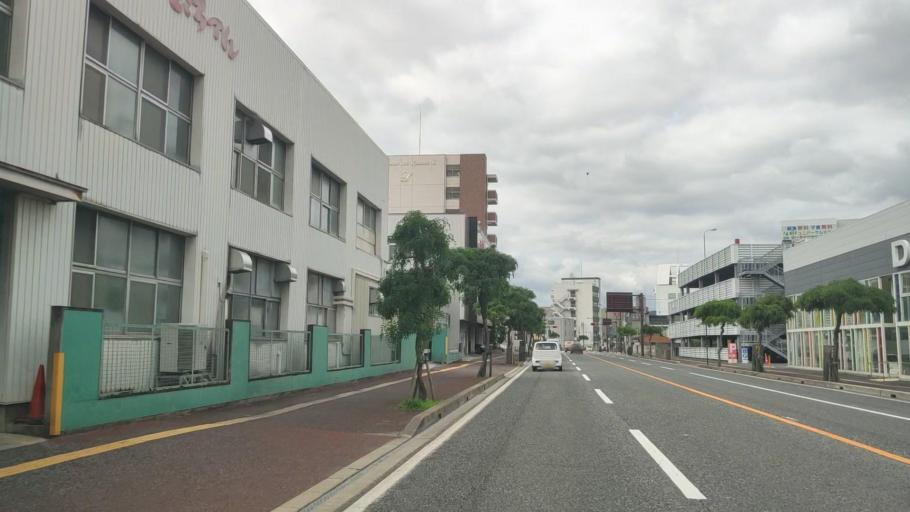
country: JP
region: Tottori
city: Yonago
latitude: 35.4275
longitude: 133.3382
